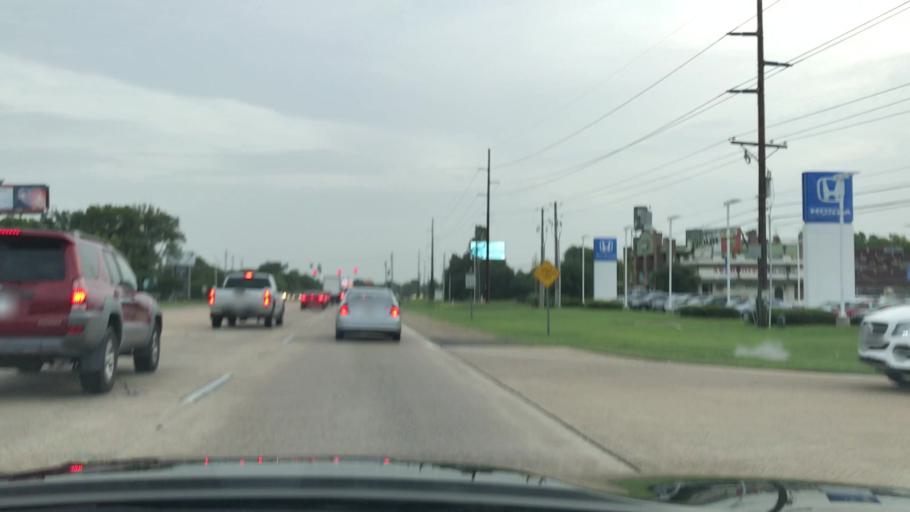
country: US
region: Louisiana
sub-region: Bossier Parish
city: Bossier City
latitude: 32.4219
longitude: -93.7206
